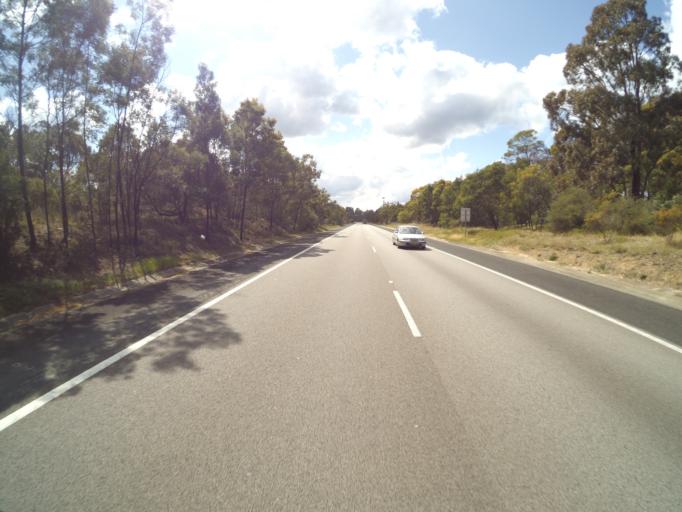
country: AU
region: New South Wales
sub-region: Wingecarribee
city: Colo Vale
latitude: -34.3736
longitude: 150.5332
